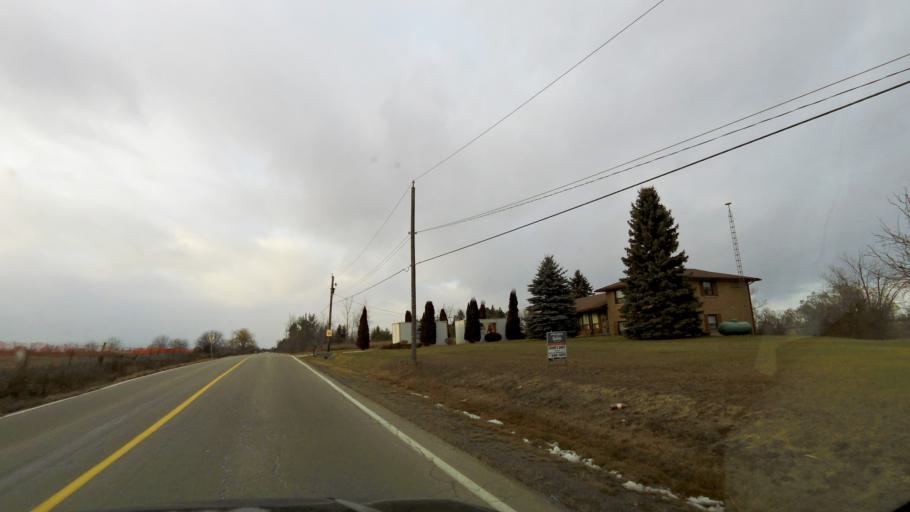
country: CA
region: Ontario
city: Brampton
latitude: 43.8214
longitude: -79.7062
